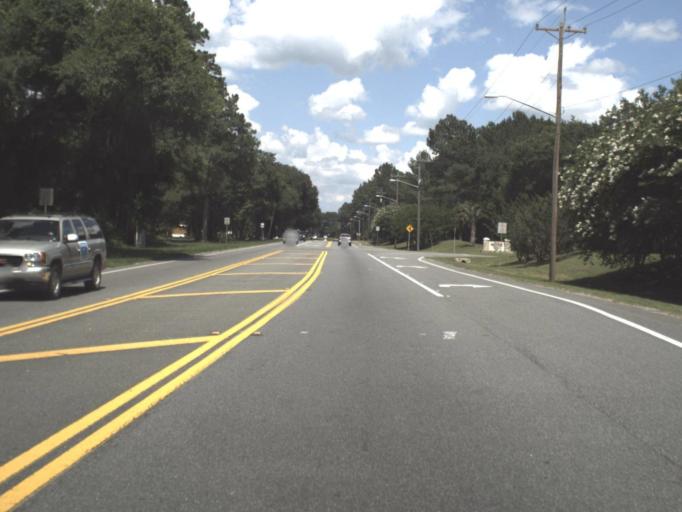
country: US
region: Florida
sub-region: Alachua County
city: Gainesville
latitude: 29.6736
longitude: -82.2651
